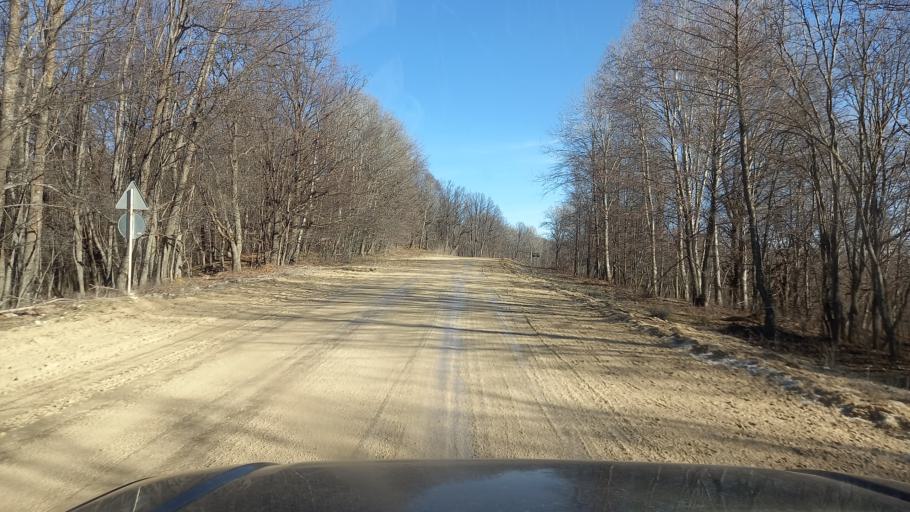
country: RU
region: Adygeya
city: Kamennomostskiy
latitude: 44.2808
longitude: 40.3105
